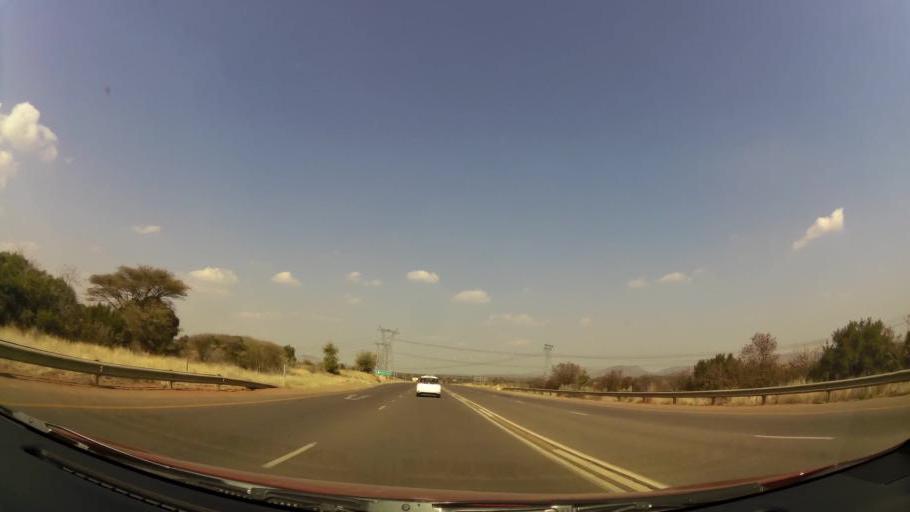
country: ZA
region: North-West
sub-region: Bojanala Platinum District Municipality
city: Mogwase
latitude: -25.3878
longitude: 27.0694
